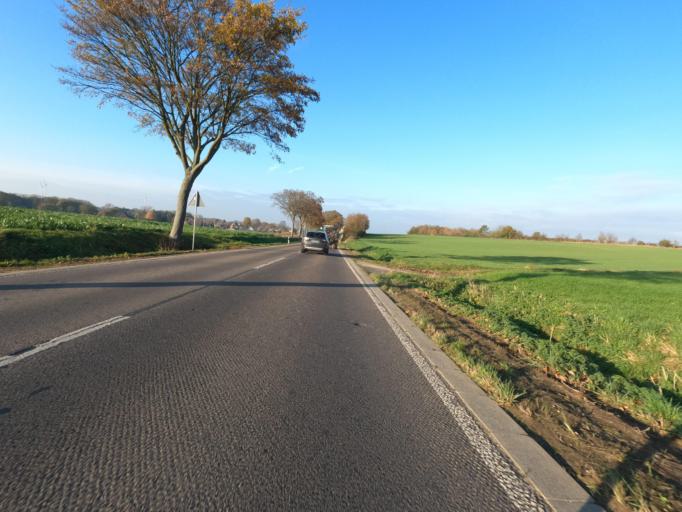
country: DE
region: North Rhine-Westphalia
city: Huckelhoven
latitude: 51.0079
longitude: 6.1917
